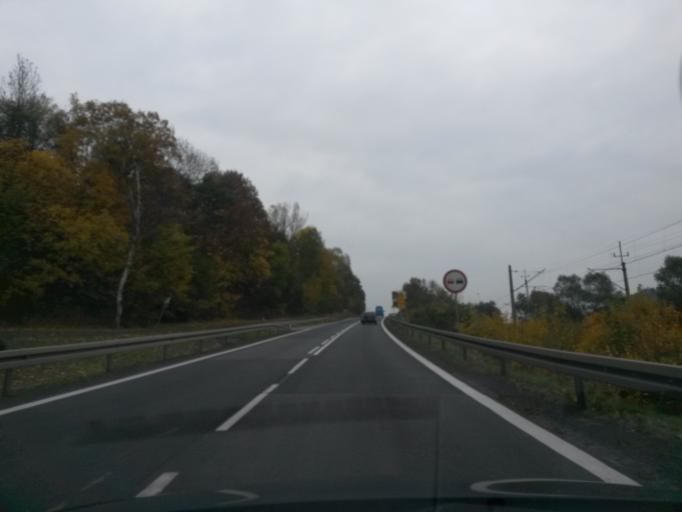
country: PL
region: Lower Silesian Voivodeship
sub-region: Powiat zabkowicki
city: Bardo
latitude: 50.5064
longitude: 16.7465
